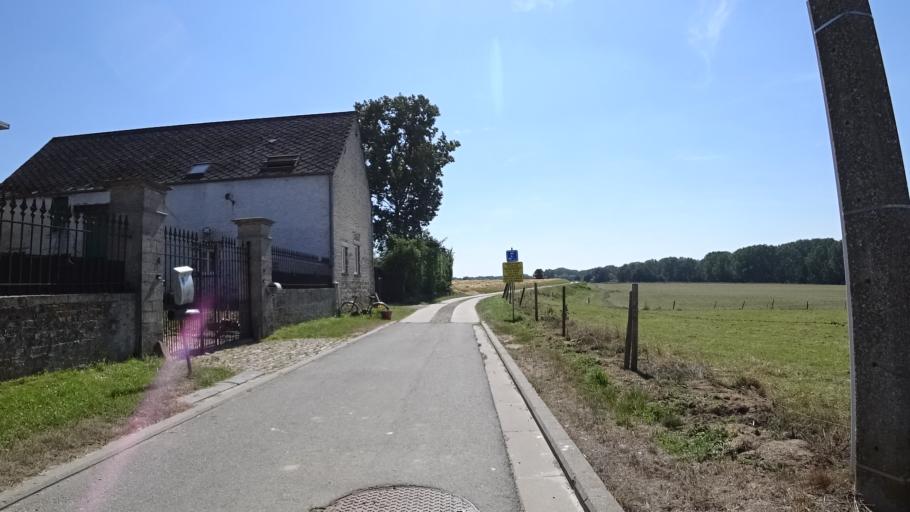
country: BE
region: Wallonia
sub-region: Province du Brabant Wallon
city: Jodoigne
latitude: 50.7036
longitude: 4.8459
